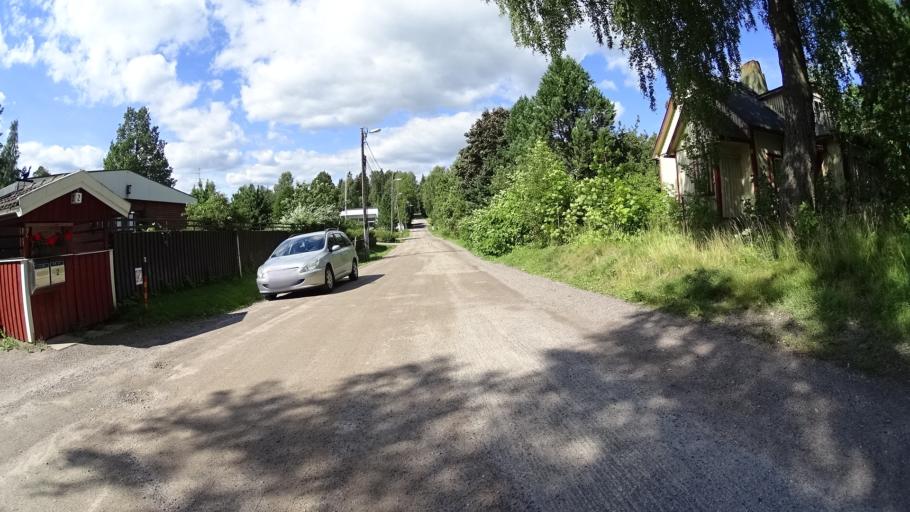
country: FI
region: Uusimaa
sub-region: Helsinki
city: Kauniainen
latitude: 60.2278
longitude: 24.7082
